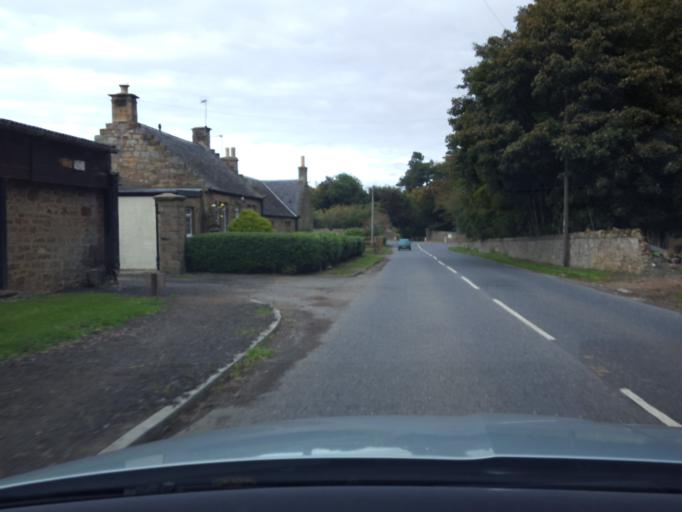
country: GB
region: Scotland
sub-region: Fife
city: Pathhead
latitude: 55.8767
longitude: -2.9868
